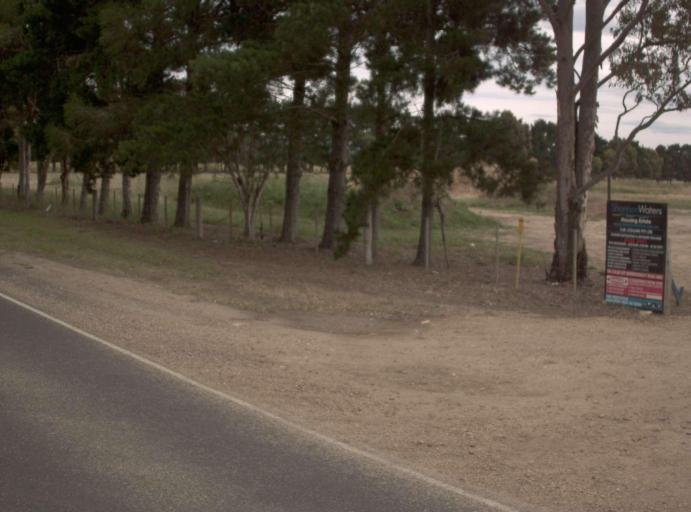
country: AU
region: Victoria
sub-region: East Gippsland
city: Bairnsdale
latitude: -37.8387
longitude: 147.5726
